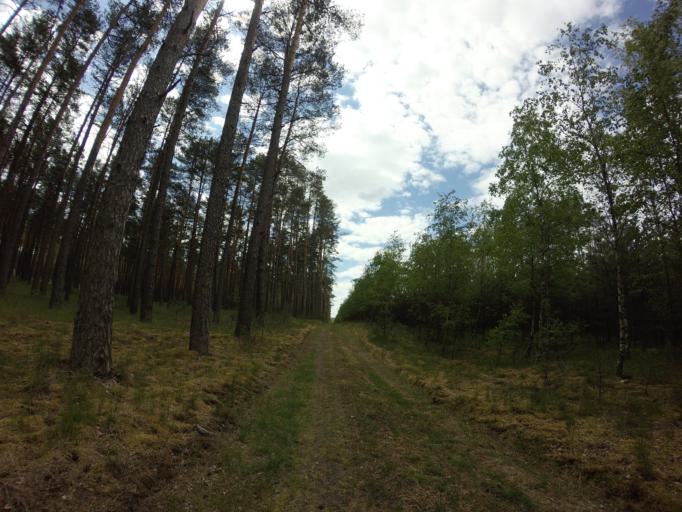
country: PL
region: West Pomeranian Voivodeship
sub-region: Powiat drawski
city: Kalisz Pomorski
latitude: 53.1623
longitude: 15.9704
